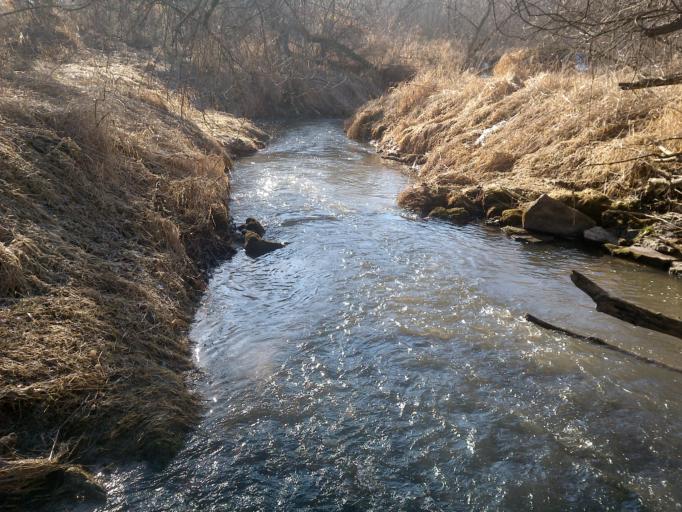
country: US
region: Minnesota
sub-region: Wabasha County
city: Lake City
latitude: 44.4385
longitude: -92.3430
